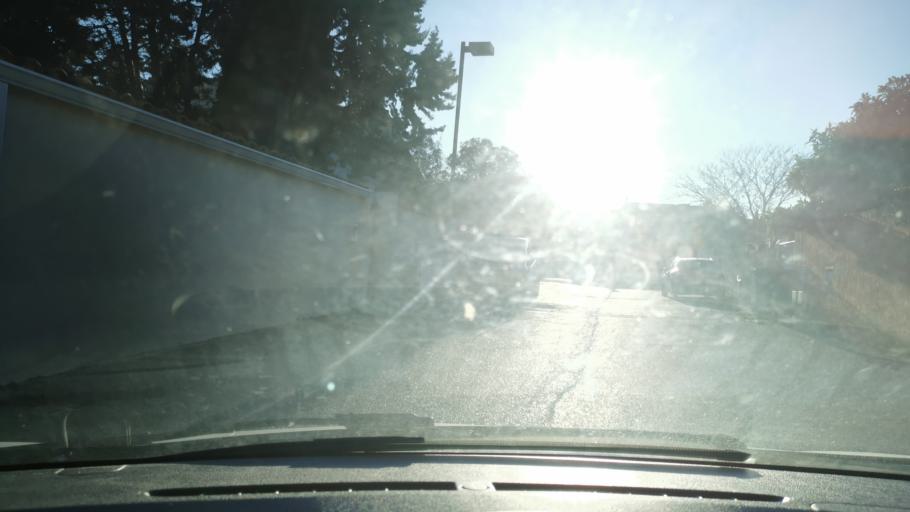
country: FR
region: Languedoc-Roussillon
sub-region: Departement de l'Herault
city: Frontignan
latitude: 43.4547
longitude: 3.7501
